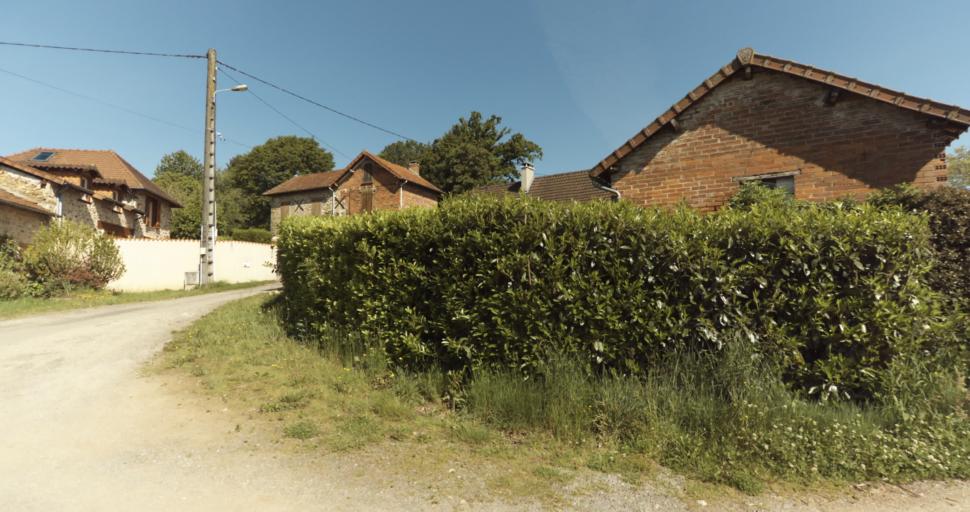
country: FR
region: Limousin
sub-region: Departement de la Haute-Vienne
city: Solignac
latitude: 45.7179
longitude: 1.2683
